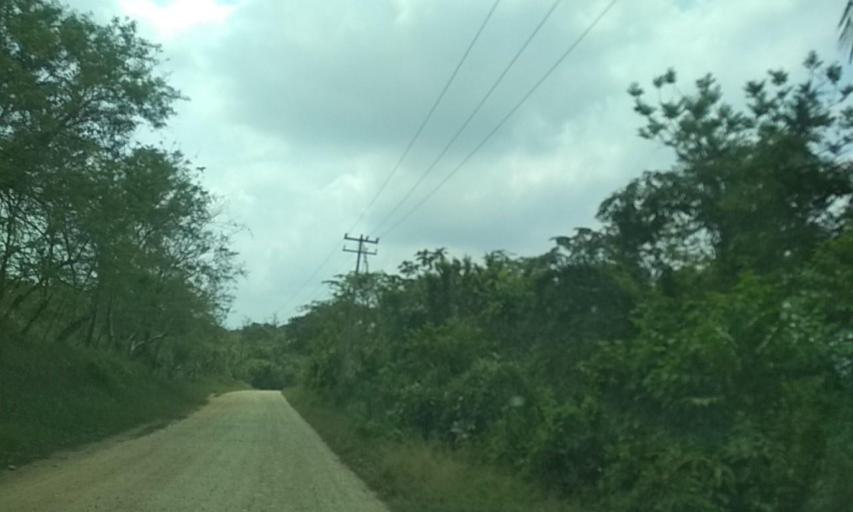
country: MX
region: Tabasco
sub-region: Huimanguillo
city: Francisco Rueda
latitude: 17.5959
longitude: -93.7953
